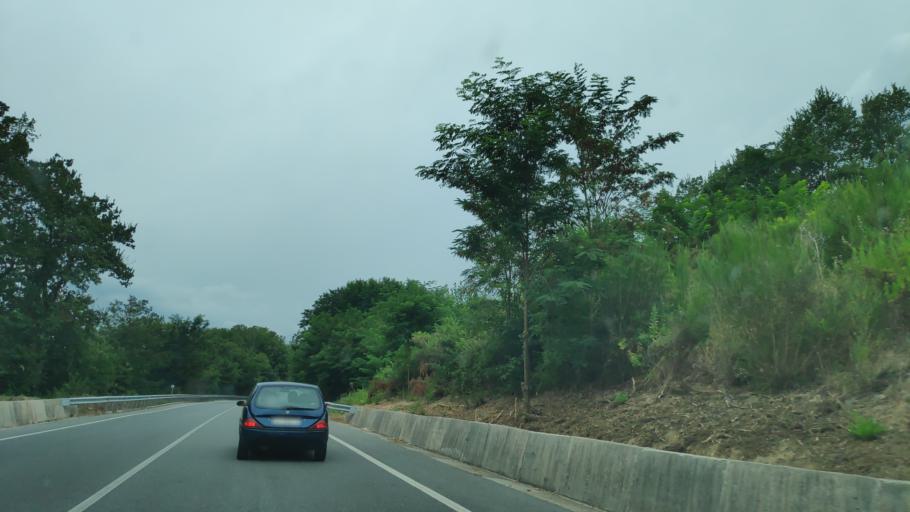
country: IT
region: Calabria
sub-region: Provincia di Catanzaro
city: Chiaravalle Centrale
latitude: 38.6692
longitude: 16.4034
